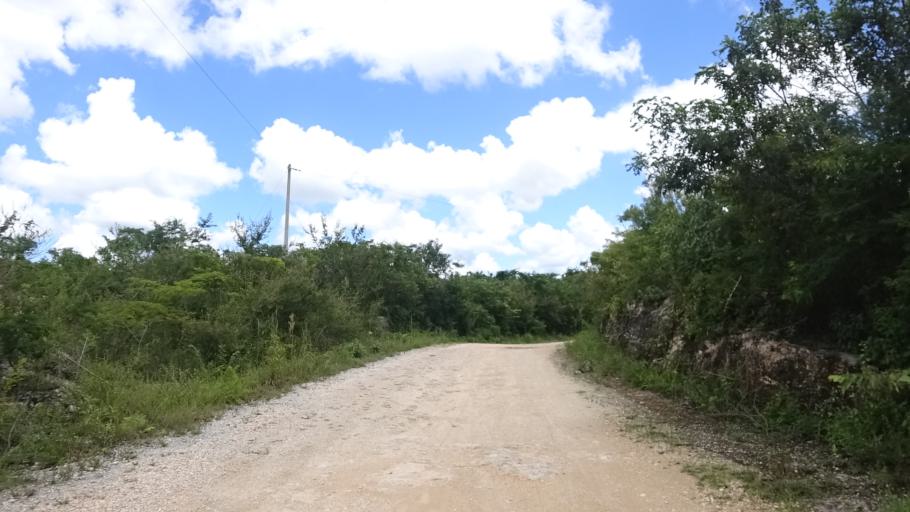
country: MX
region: Yucatan
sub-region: Valladolid
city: Dzitnup
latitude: 20.6723
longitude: -88.2282
